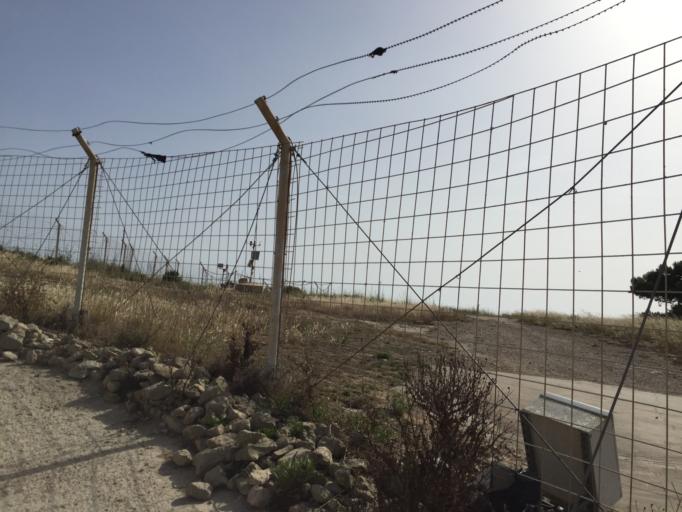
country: MT
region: Il-Qrendi
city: Qrendi
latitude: 35.8275
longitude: 14.4427
